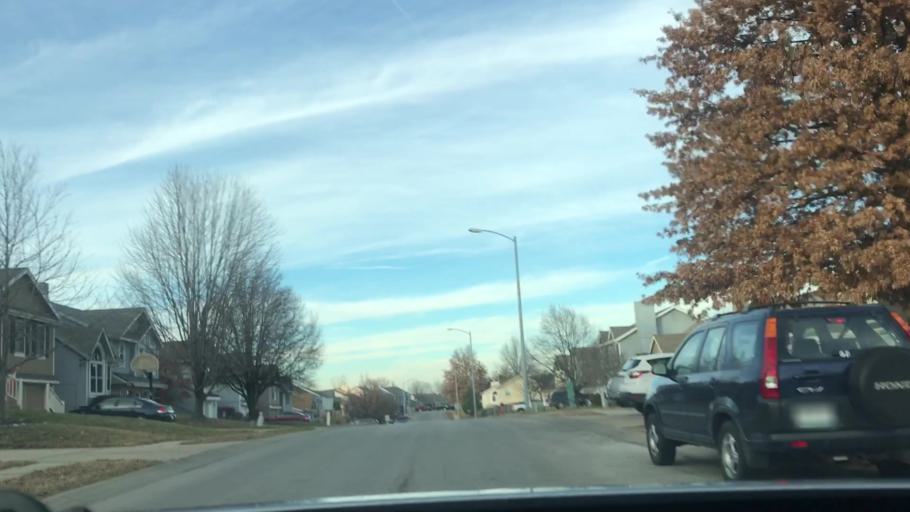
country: US
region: Missouri
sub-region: Platte County
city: Riverside
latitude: 39.2038
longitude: -94.5966
